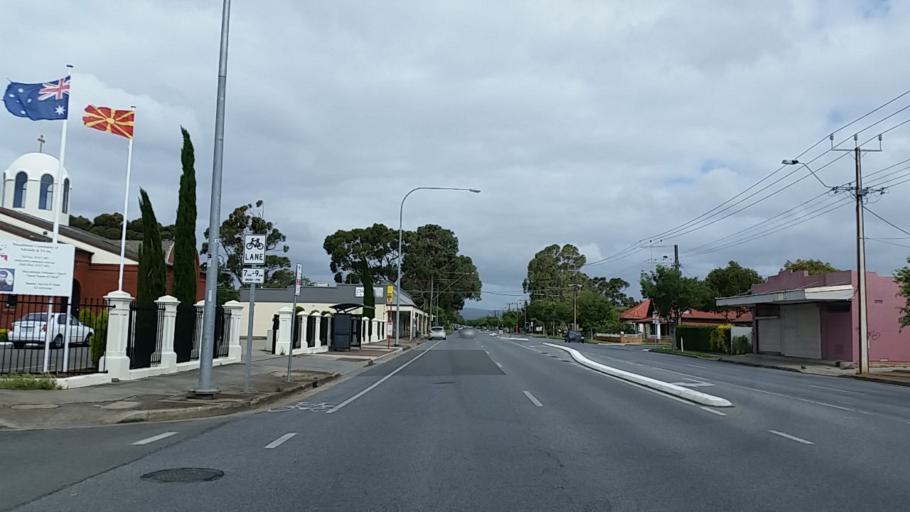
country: AU
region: South Australia
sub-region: Charles Sturt
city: Findon
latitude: -34.8974
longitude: 138.5353
